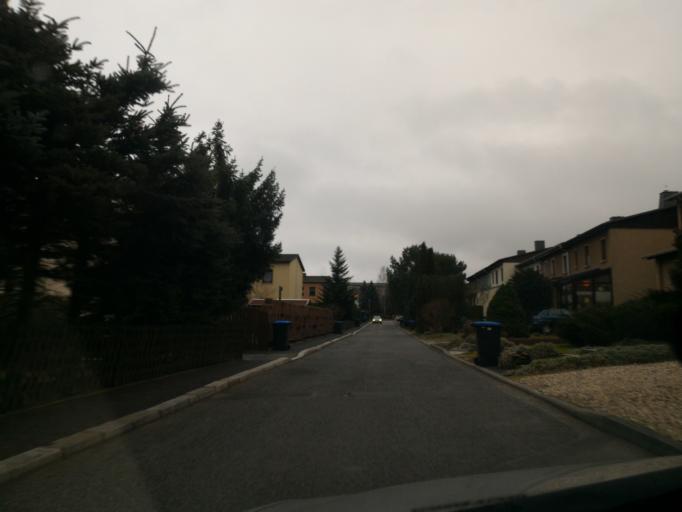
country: DE
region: Saxony
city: Grossschonau
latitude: 50.8913
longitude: 14.6664
